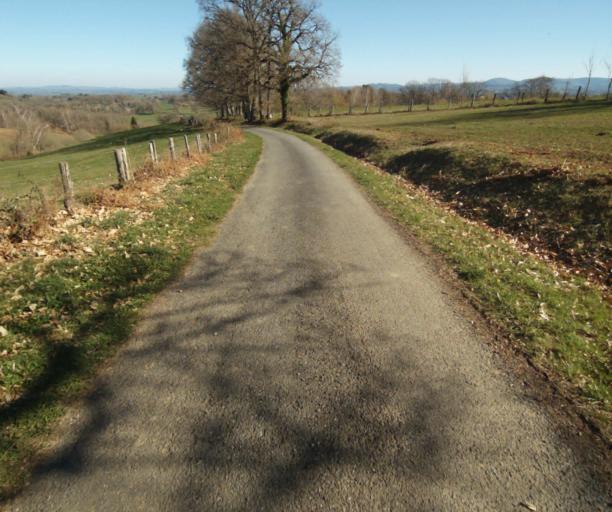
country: FR
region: Limousin
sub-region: Departement de la Correze
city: Seilhac
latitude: 45.3934
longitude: 1.6981
